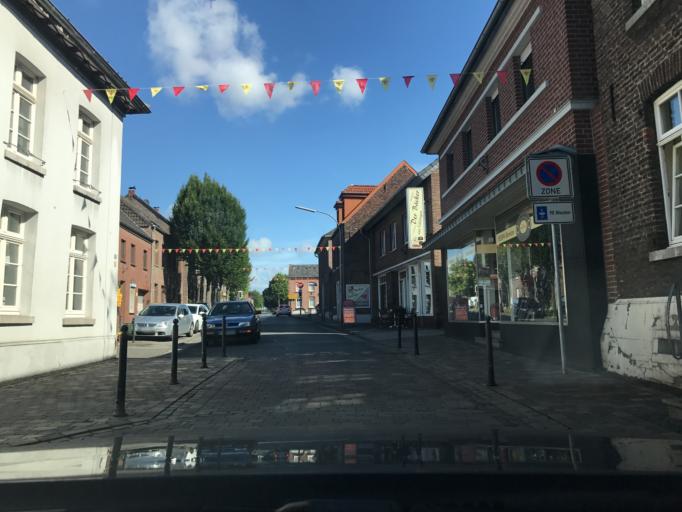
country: DE
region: North Rhine-Westphalia
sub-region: Regierungsbezirk Dusseldorf
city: Wachtendonk
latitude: 51.4005
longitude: 6.3068
